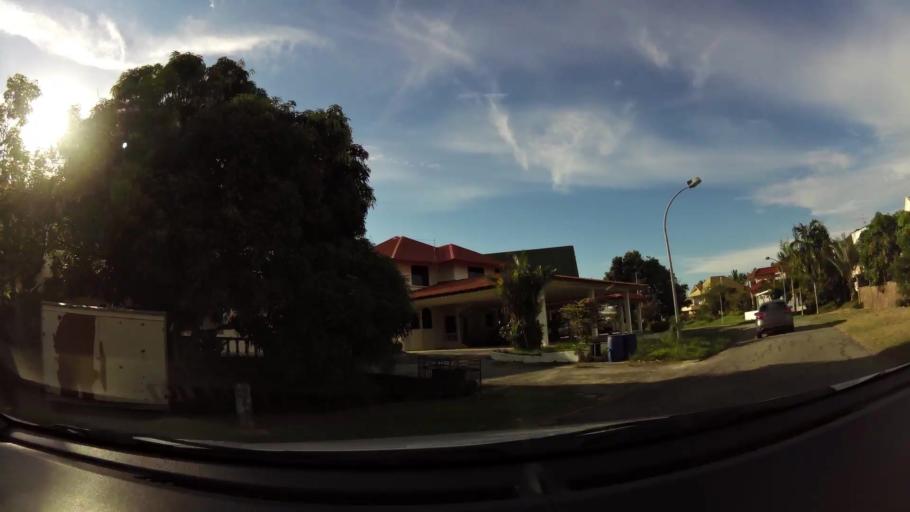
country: BN
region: Brunei and Muara
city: Bandar Seri Begawan
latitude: 4.9854
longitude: 114.9705
